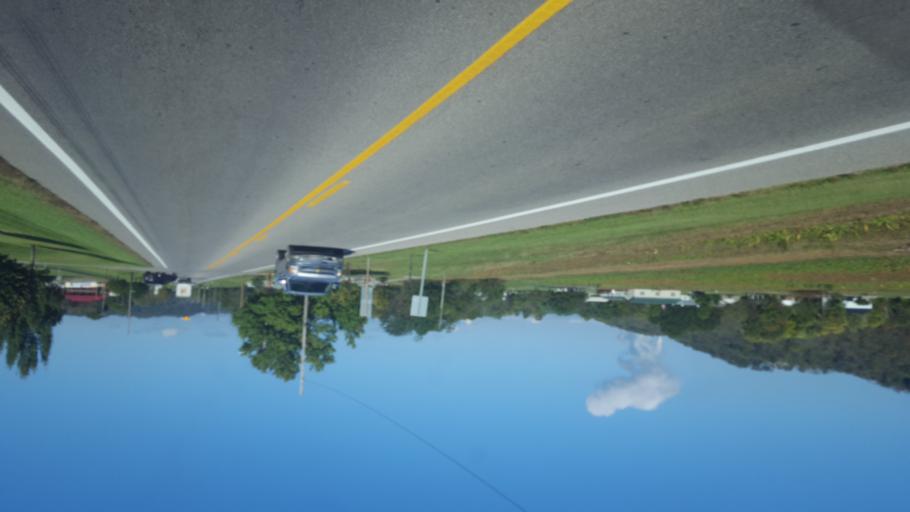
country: US
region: Ohio
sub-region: Brown County
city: Aberdeen
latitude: 38.6691
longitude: -83.7722
